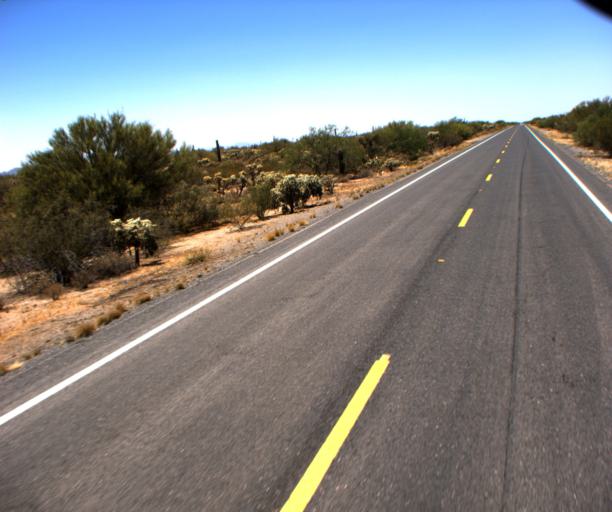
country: US
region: Arizona
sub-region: Pinal County
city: Florence
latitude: 32.8091
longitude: -111.1911
